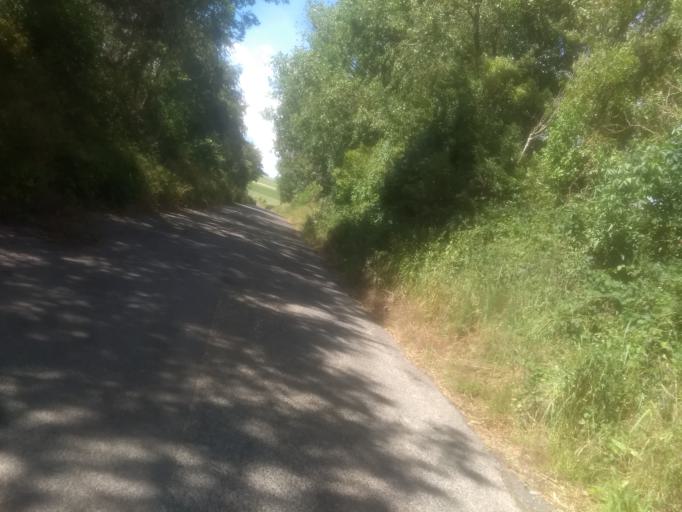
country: FR
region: Nord-Pas-de-Calais
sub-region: Departement du Pas-de-Calais
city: Tilloy-les-Mofflaines
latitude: 50.2504
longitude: 2.8238
